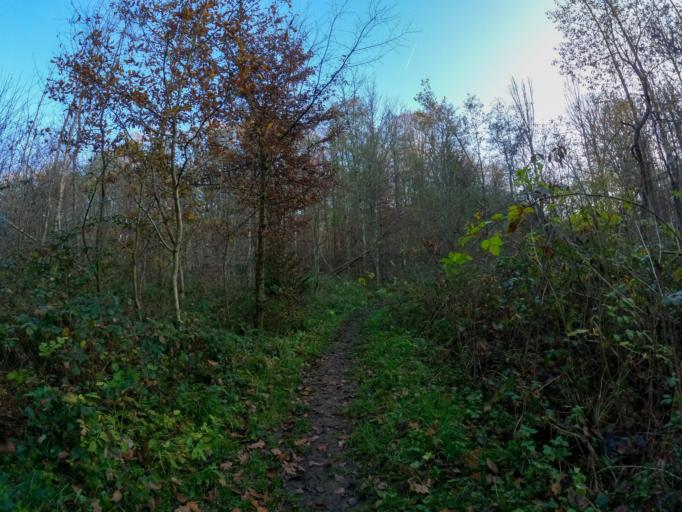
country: LU
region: Luxembourg
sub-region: Canton de Capellen
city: Dippach
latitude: 49.6038
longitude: 6.0066
